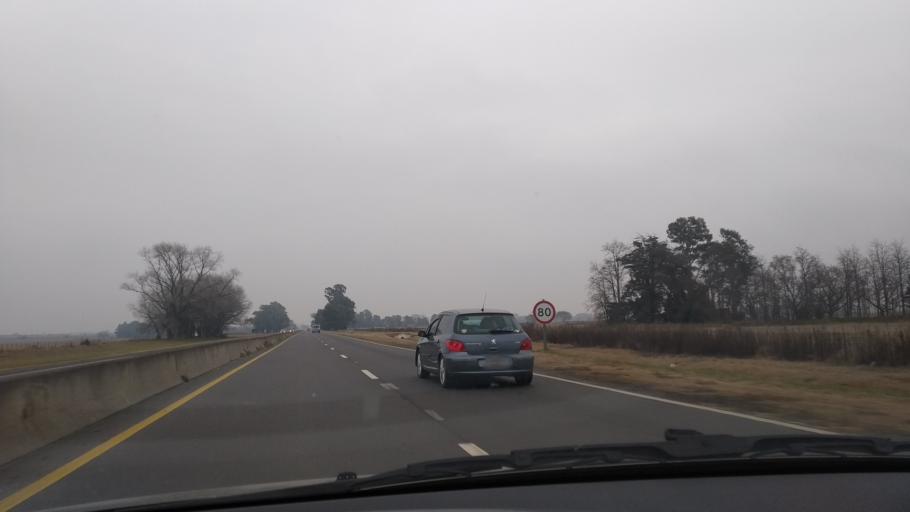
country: AR
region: Buenos Aires
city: Olavarria
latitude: -36.8662
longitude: -60.1285
